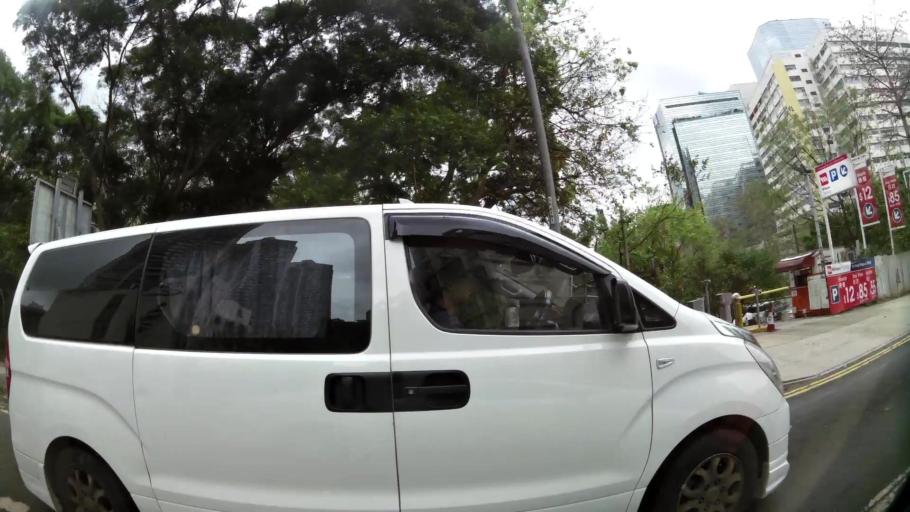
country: HK
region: Wong Tai Sin
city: Wong Tai Sin
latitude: 22.3401
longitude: 114.1982
